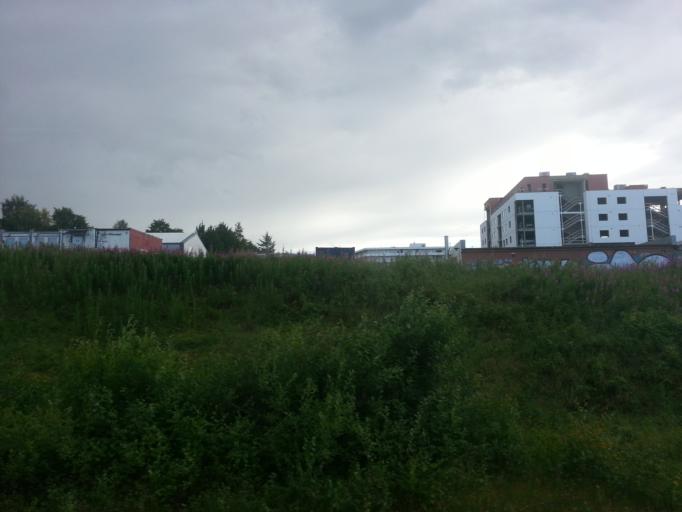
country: NO
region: Sor-Trondelag
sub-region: Trondheim
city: Trondheim
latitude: 63.4385
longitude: 10.4585
